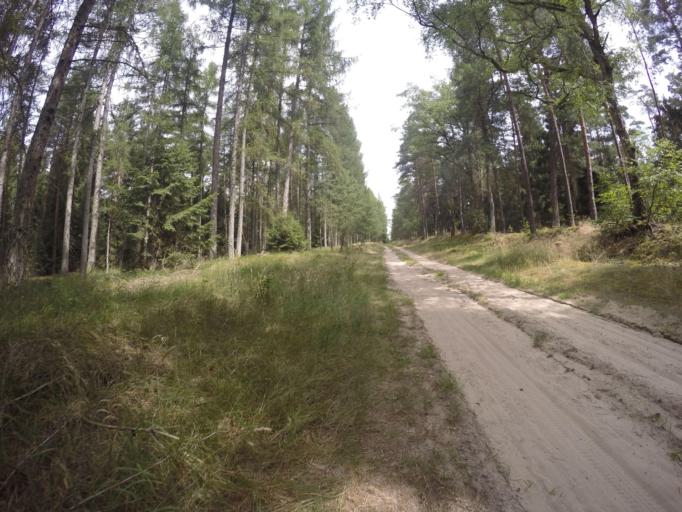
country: DE
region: Lower Saxony
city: Thomasburg
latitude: 53.2477
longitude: 10.6775
